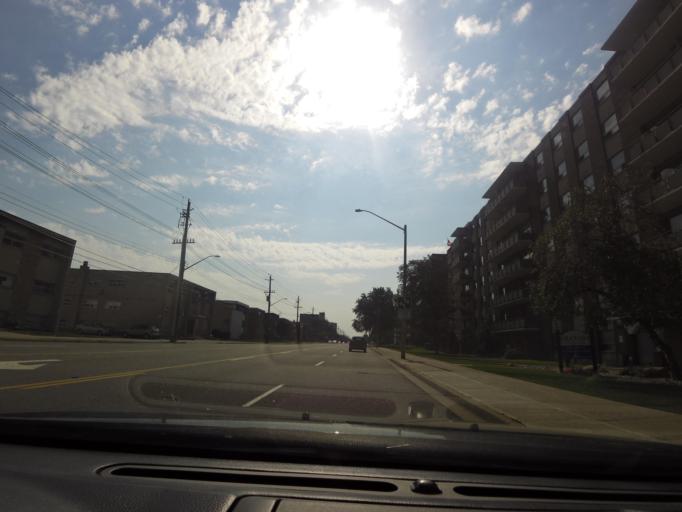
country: CA
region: Ontario
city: Hamilton
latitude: 43.2259
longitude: -79.8708
